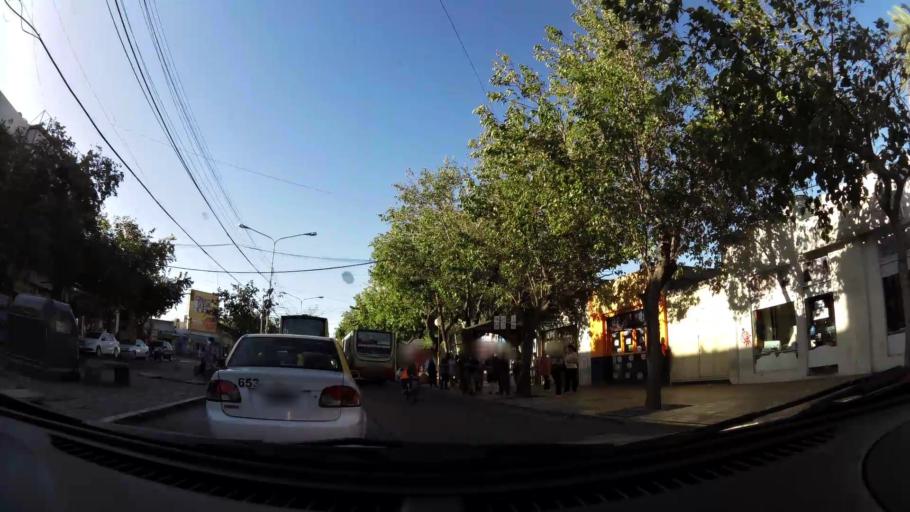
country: AR
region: San Juan
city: San Juan
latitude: -31.5344
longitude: -68.5216
